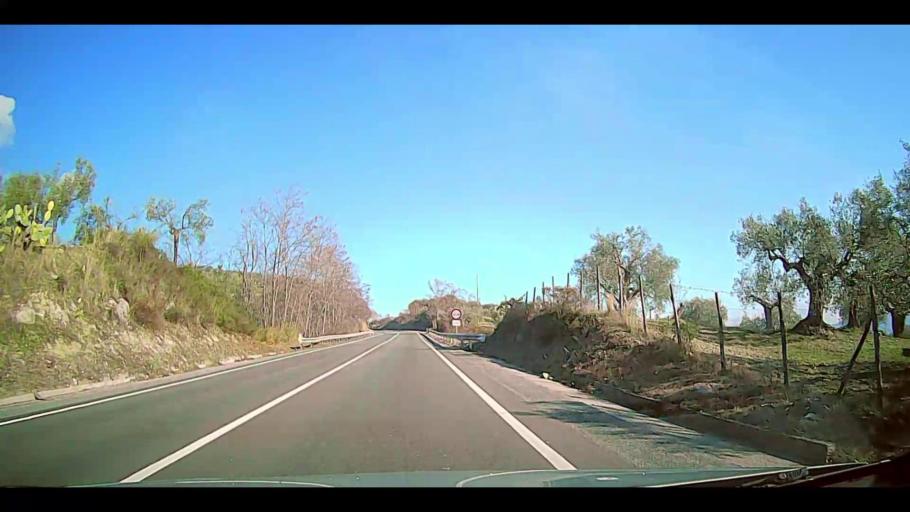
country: IT
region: Calabria
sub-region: Provincia di Crotone
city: Caccuri
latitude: 39.2132
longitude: 16.7968
